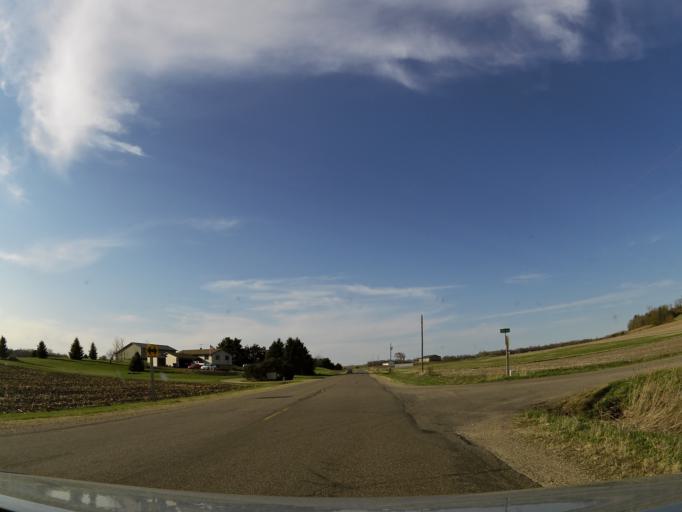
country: US
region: Wisconsin
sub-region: Pierce County
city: River Falls
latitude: 44.7672
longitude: -92.6397
